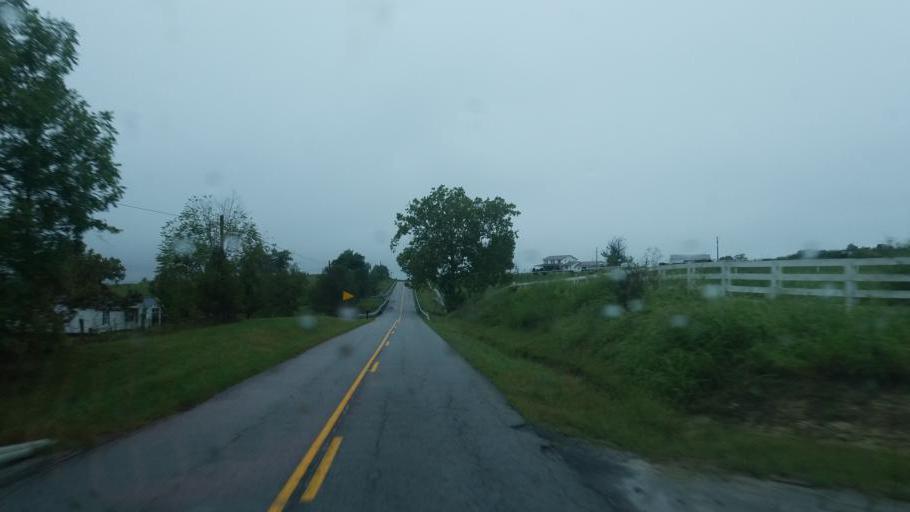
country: US
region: Kentucky
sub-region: Fleming County
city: Flemingsburg
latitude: 38.4138
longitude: -83.6795
